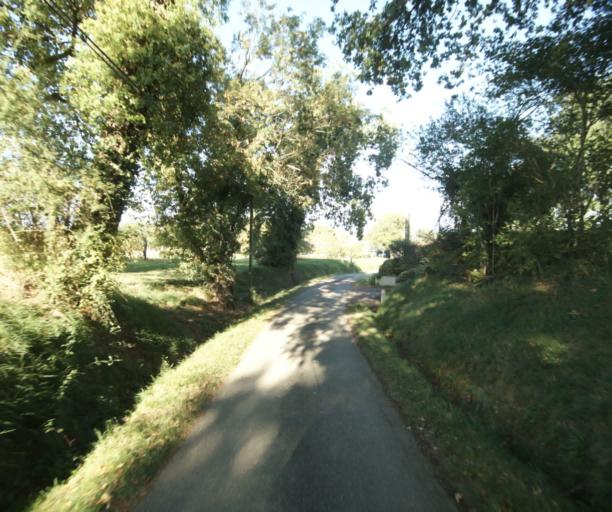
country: FR
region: Midi-Pyrenees
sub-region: Departement du Gers
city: Eauze
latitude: 43.8028
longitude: 0.1297
